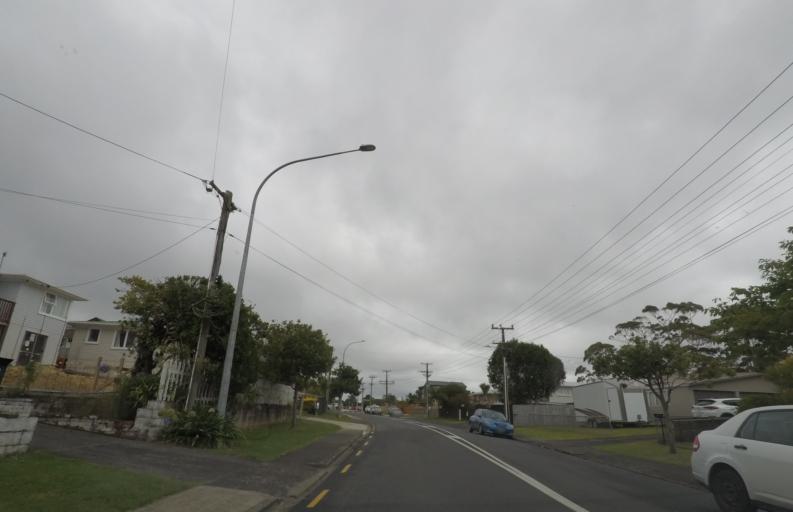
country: NZ
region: Auckland
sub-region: Auckland
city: Rosebank
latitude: -36.8651
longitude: 174.6385
